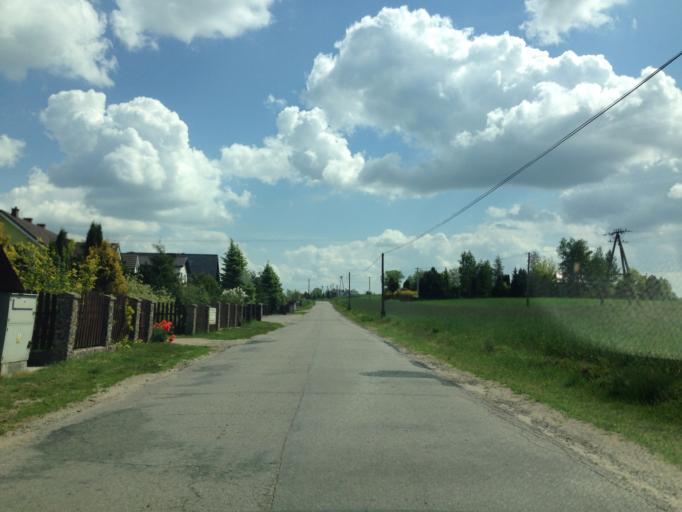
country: PL
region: Kujawsko-Pomorskie
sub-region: Powiat brodnicki
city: Brodnica
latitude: 53.3347
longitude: 19.3626
